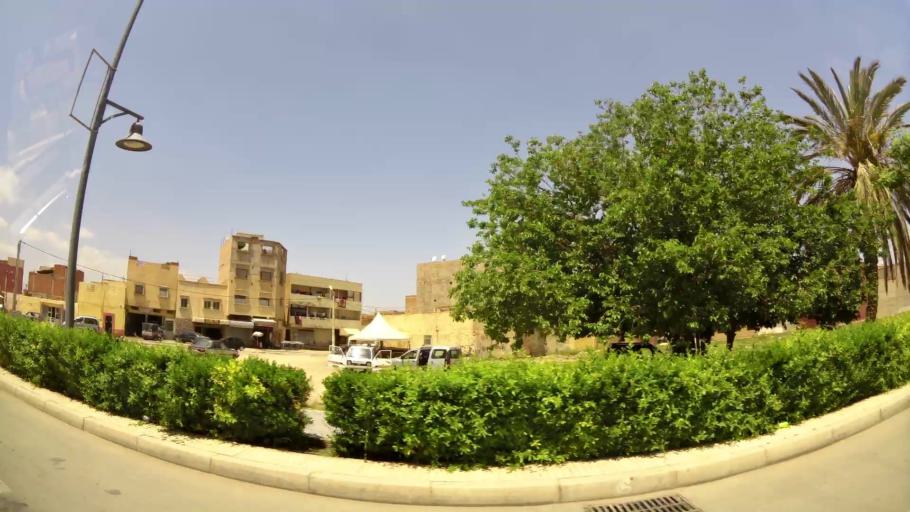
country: MA
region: Oriental
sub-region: Oujda-Angad
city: Oujda
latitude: 34.6798
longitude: -1.8924
